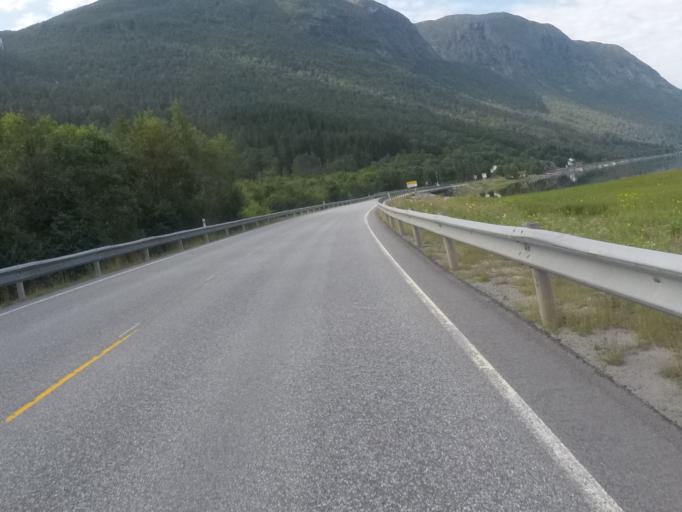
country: NO
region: More og Romsdal
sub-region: Rauma
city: Andalsnes
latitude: 62.5727
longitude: 7.7874
